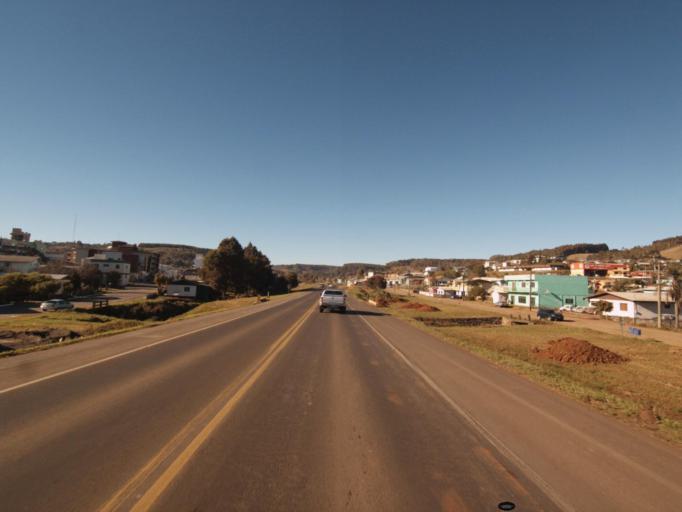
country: BR
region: Santa Catarina
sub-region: Concordia
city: Concordia
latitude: -26.8702
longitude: -52.0203
